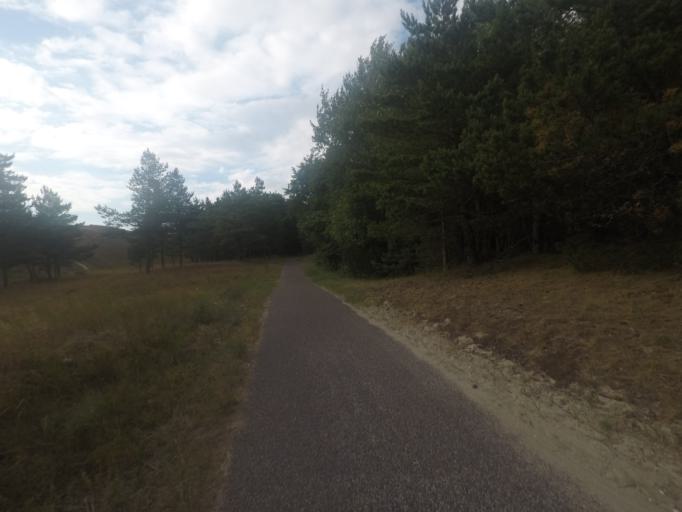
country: LT
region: Klaipedos apskritis
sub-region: Klaipeda
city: Klaipeda
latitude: 55.6581
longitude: 21.1070
